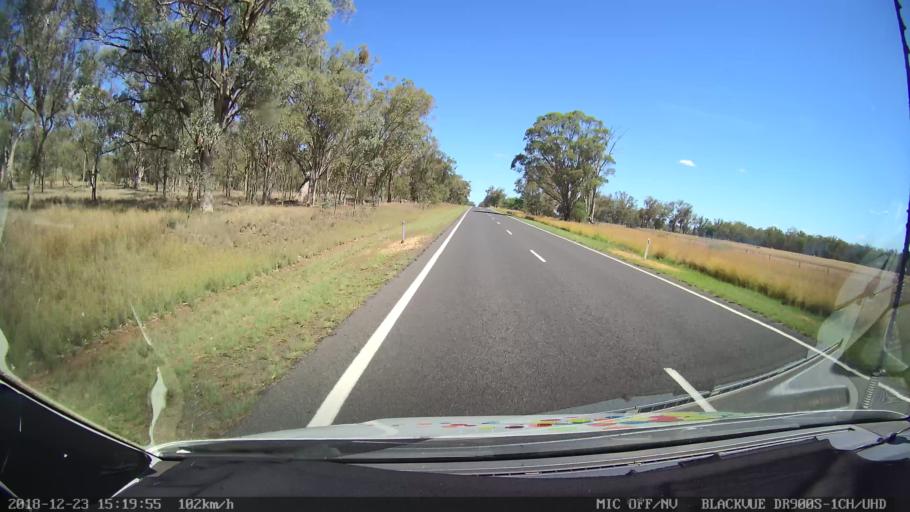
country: AU
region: New South Wales
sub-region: Tamworth Municipality
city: Manilla
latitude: -30.8356
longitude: 150.7861
